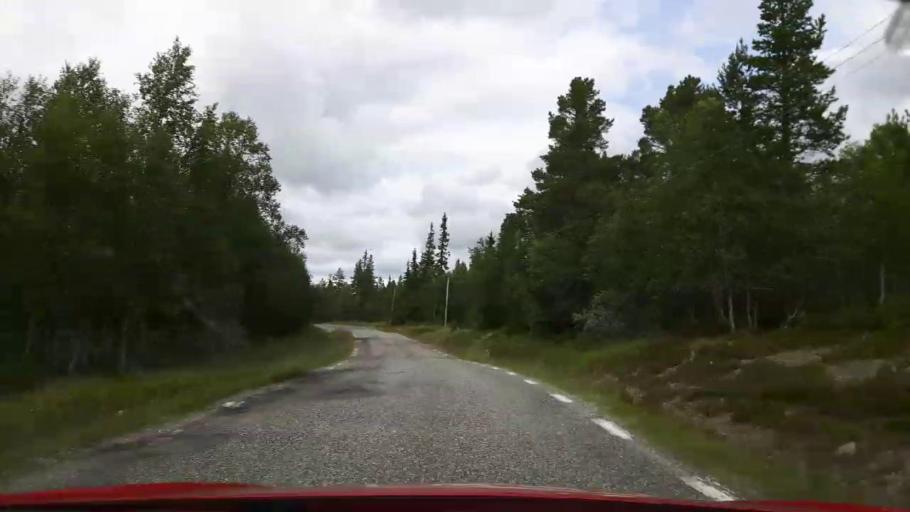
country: NO
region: Hedmark
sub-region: Engerdal
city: Engerdal
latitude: 62.3115
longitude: 12.8101
